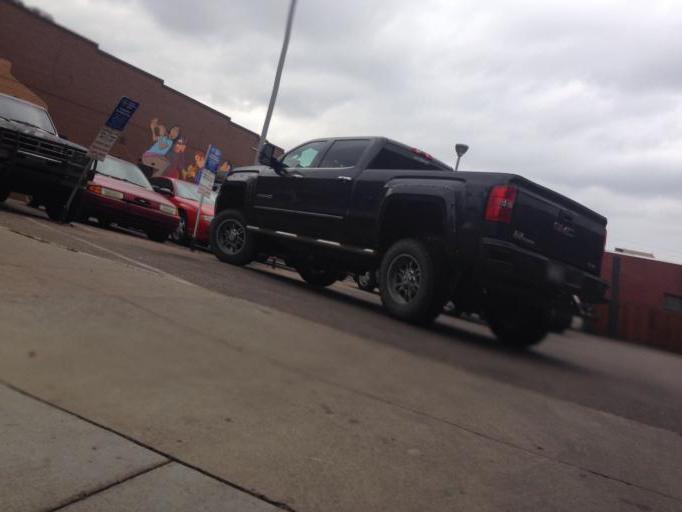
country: US
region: Colorado
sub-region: Larimer County
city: Fort Collins
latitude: 40.5856
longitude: -105.0779
